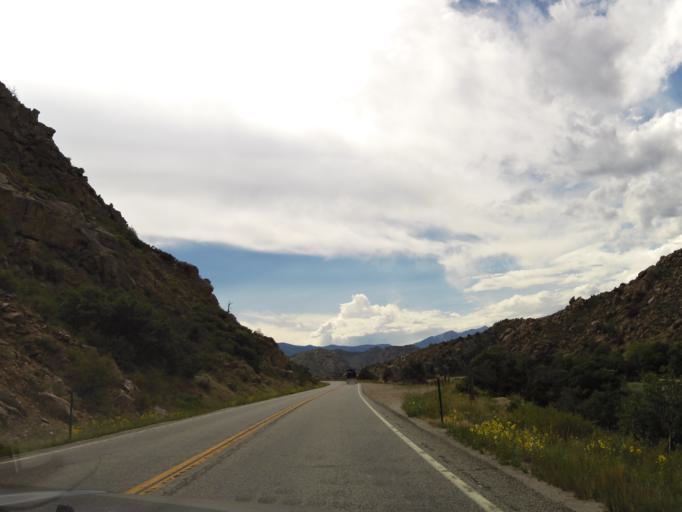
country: US
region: Colorado
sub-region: Custer County
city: Westcliffe
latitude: 38.3851
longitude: -105.6593
